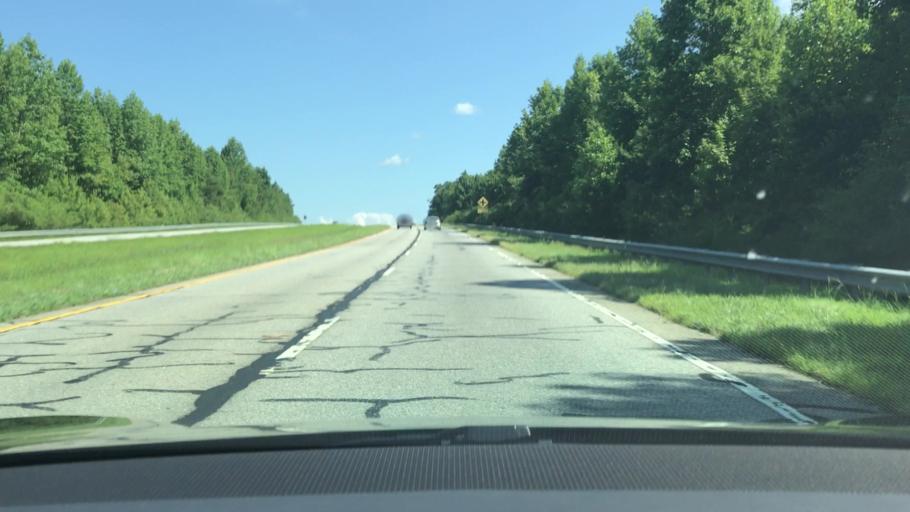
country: US
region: Georgia
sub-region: Habersham County
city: Clarkesville
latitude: 34.6221
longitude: -83.4471
